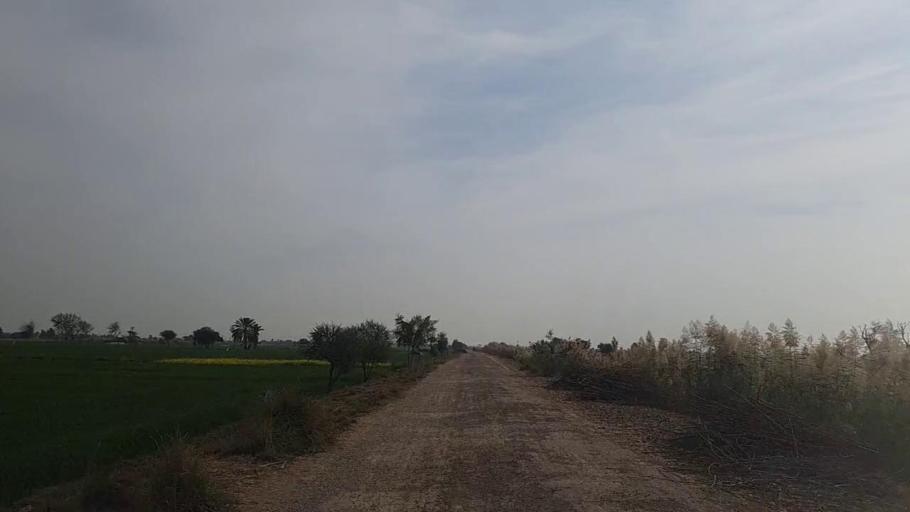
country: PK
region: Sindh
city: Daur
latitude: 26.4474
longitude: 68.4175
